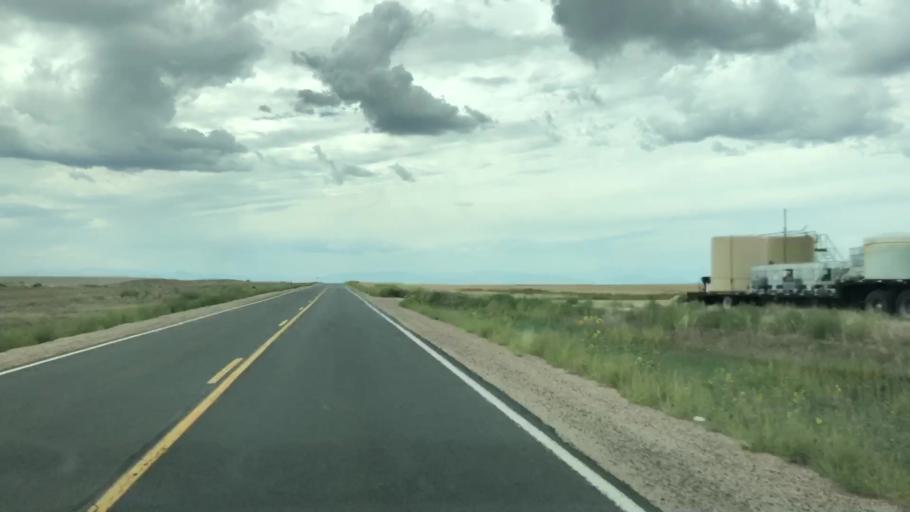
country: US
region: Colorado
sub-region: Adams County
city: Aurora
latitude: 39.7984
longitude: -104.7010
